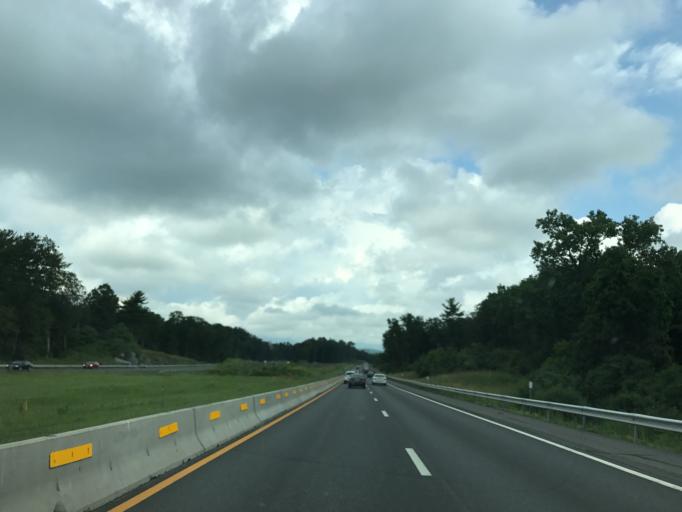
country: US
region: New York
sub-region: Greene County
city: Jefferson Heights
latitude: 42.2850
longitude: -73.8730
